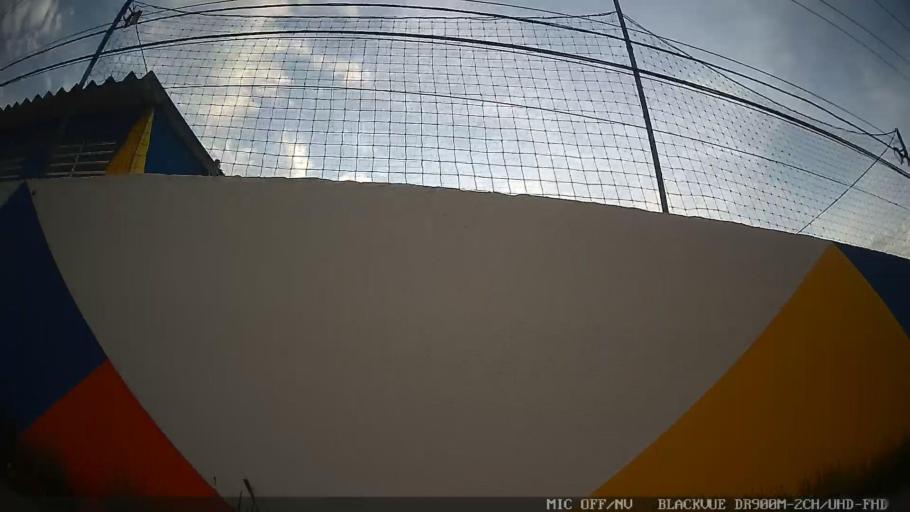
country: BR
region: Sao Paulo
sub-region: Cubatao
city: Cubatao
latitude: -23.8944
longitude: -46.4305
